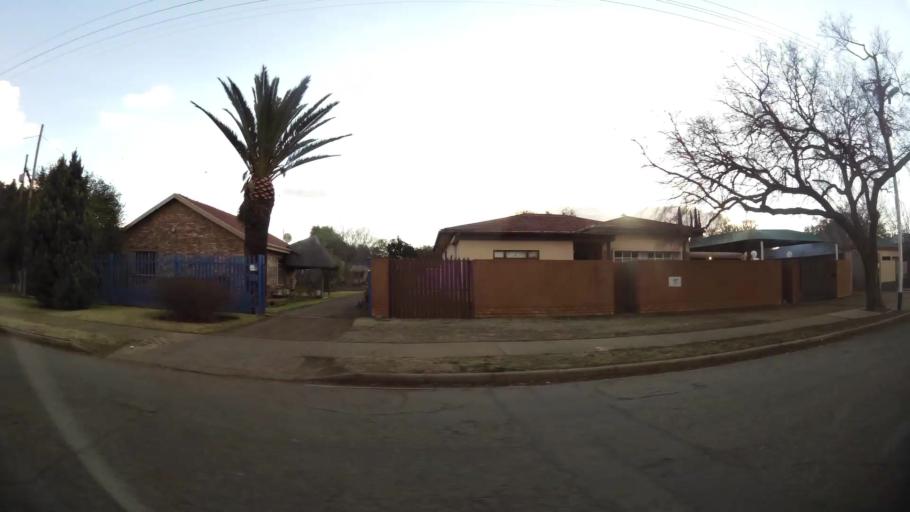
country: ZA
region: North-West
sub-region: Dr Kenneth Kaunda District Municipality
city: Potchefstroom
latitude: -26.7366
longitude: 27.0908
